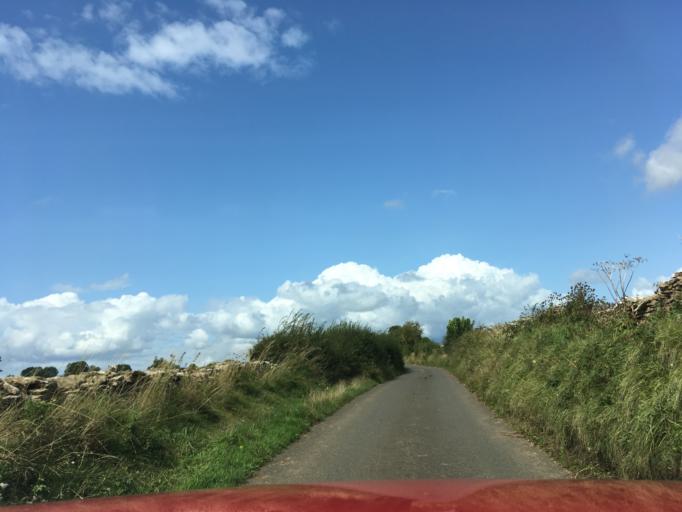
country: GB
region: England
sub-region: Wiltshire
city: Luckington
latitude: 51.6110
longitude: -2.2530
